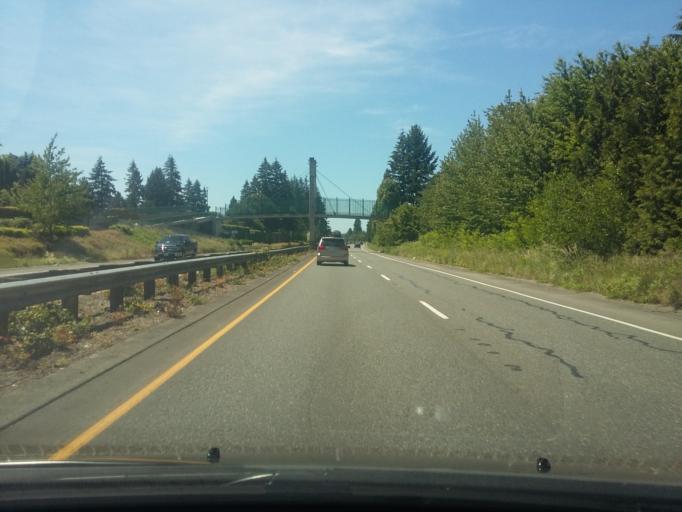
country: US
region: Washington
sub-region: Clark County
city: Orchards
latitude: 45.6829
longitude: -122.5253
